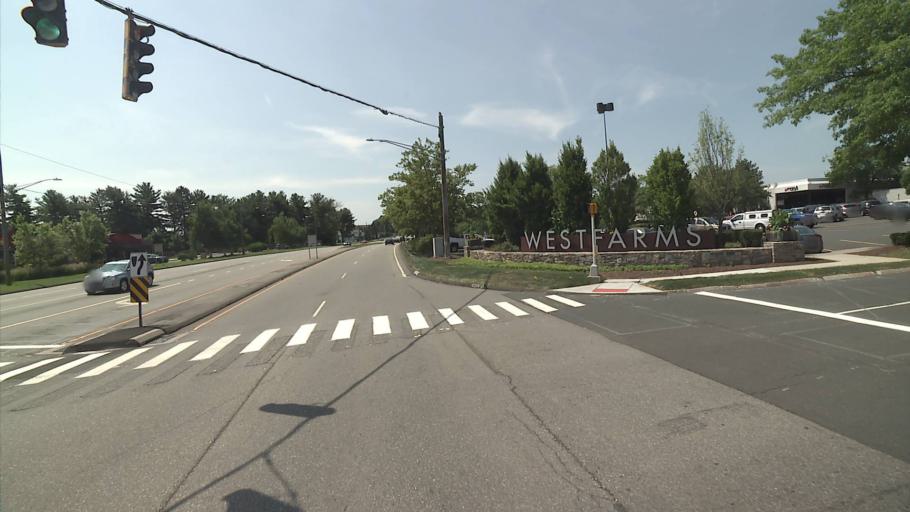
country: US
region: Connecticut
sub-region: Hartford County
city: West Hartford
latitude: 41.7238
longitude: -72.7603
